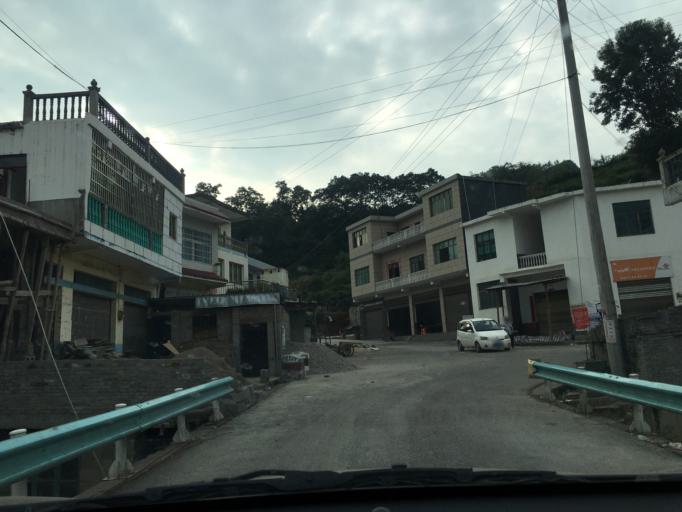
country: CN
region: Guangxi Zhuangzu Zizhiqu
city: Xinzhou
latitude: 25.4357
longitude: 105.4775
